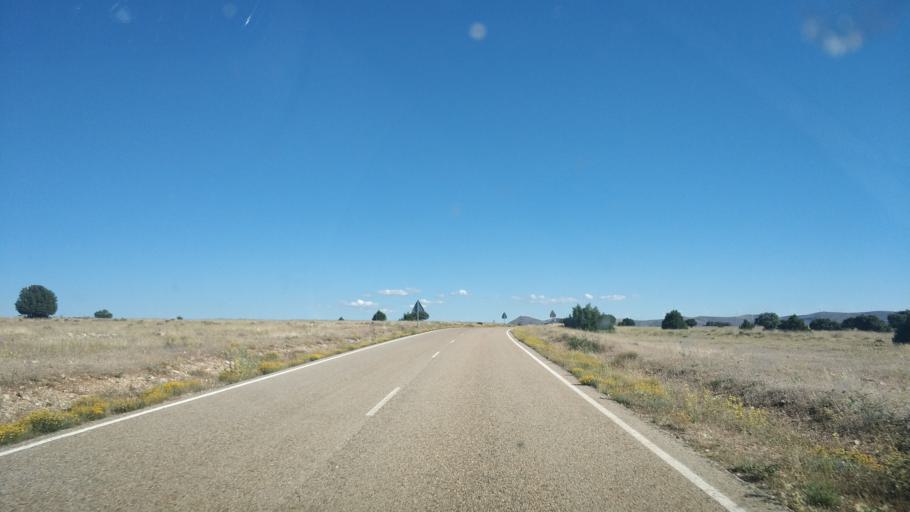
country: ES
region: Castille and Leon
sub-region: Provincia de Soria
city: Montejo de Tiermes
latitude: 41.3858
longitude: -3.1944
